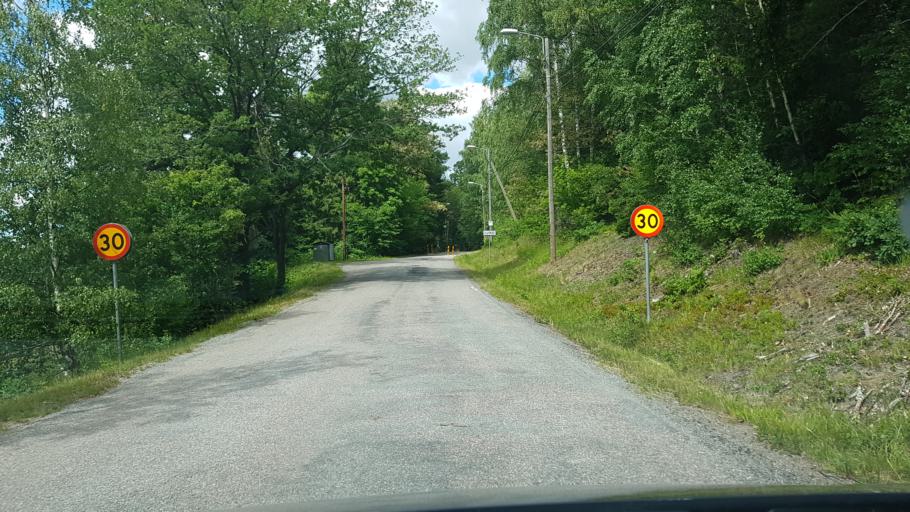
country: SE
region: Stockholm
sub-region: Upplands-Bro Kommun
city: Kungsaengen
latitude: 59.4904
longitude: 17.8042
